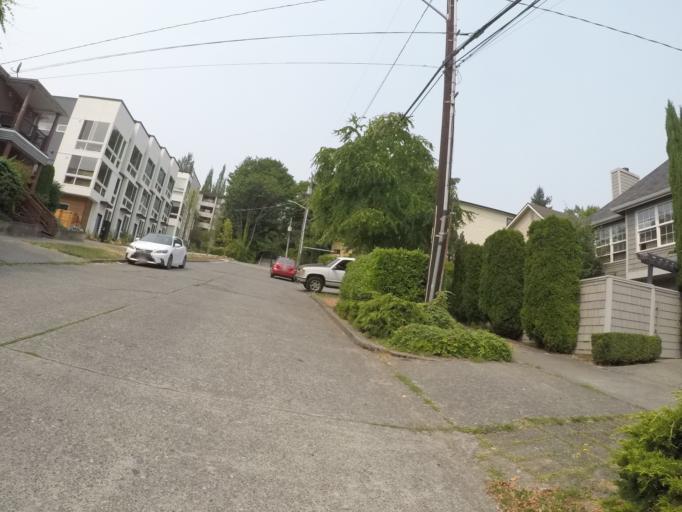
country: US
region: Washington
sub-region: King County
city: Seattle
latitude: 47.6214
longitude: -122.2976
